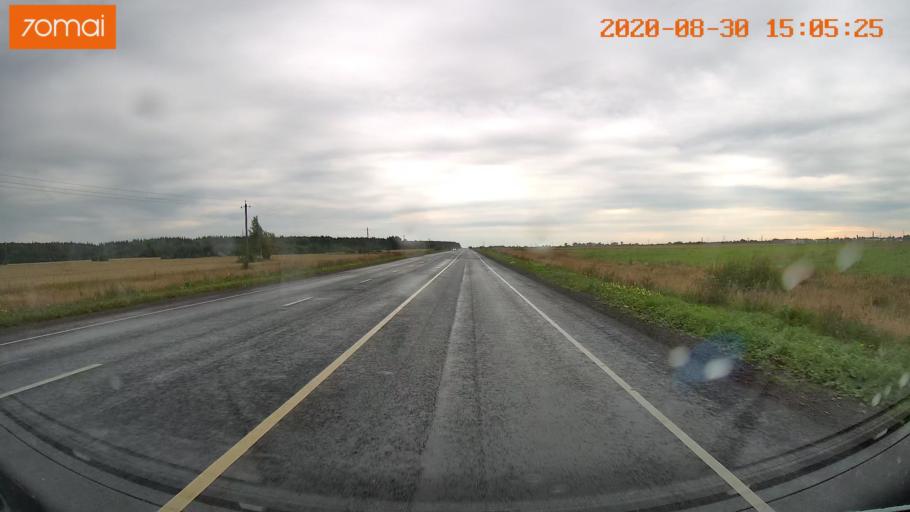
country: RU
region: Ivanovo
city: Staraya Vichuga
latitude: 57.2714
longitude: 41.9070
